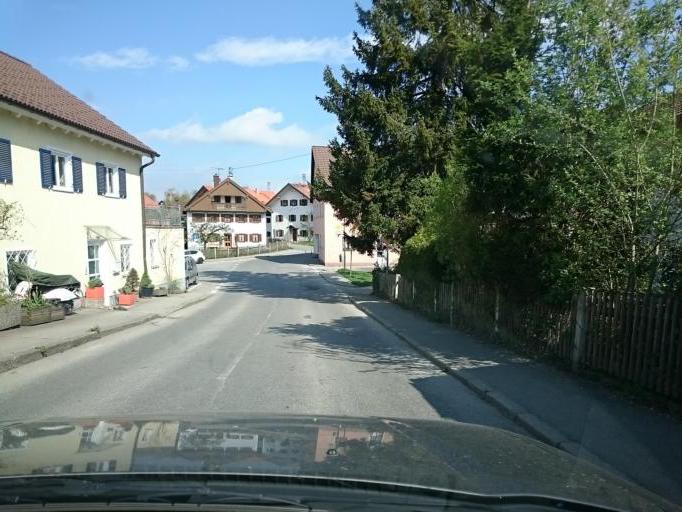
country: DE
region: Bavaria
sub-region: Upper Bavaria
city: Murnau am Staffelsee
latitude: 47.6785
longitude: 11.2051
